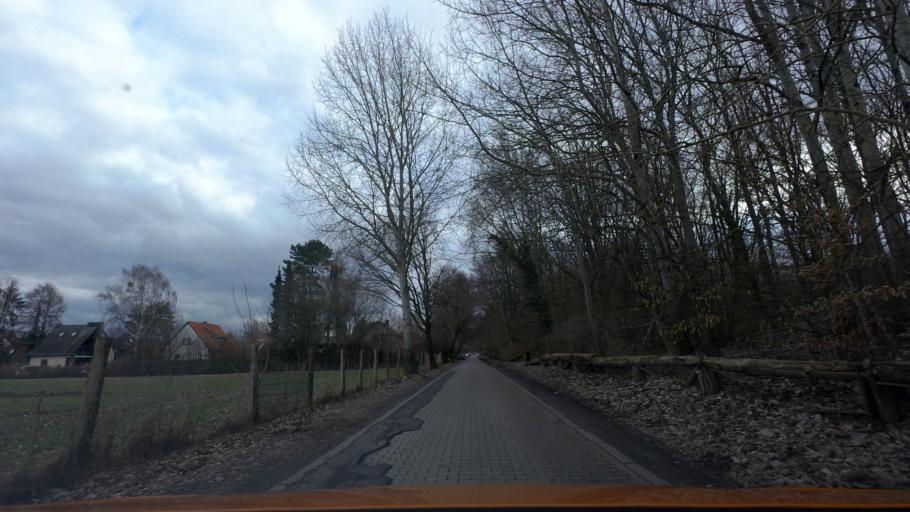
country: DE
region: Berlin
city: Konradshohe
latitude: 52.5994
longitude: 13.2347
